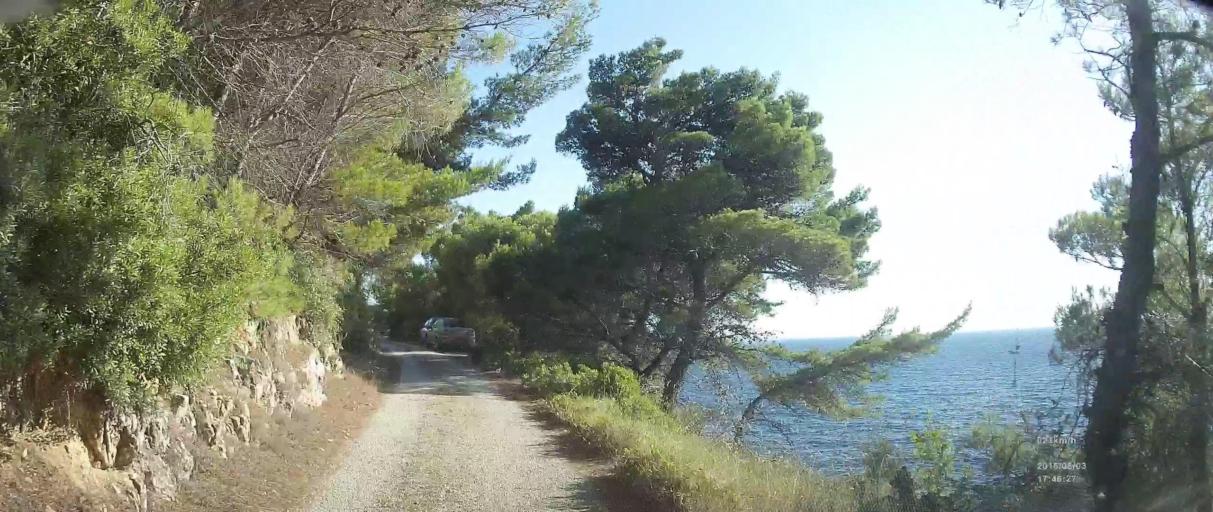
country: HR
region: Dubrovacko-Neretvanska
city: Blato
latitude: 42.7399
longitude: 17.4991
